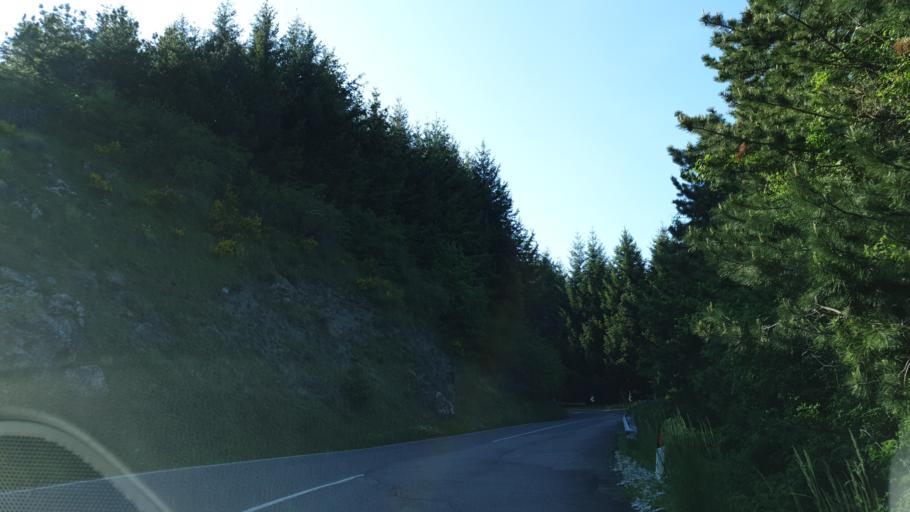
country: IT
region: Tuscany
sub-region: Province of Arezzo
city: Montemignaio
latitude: 43.7853
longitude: 11.6136
